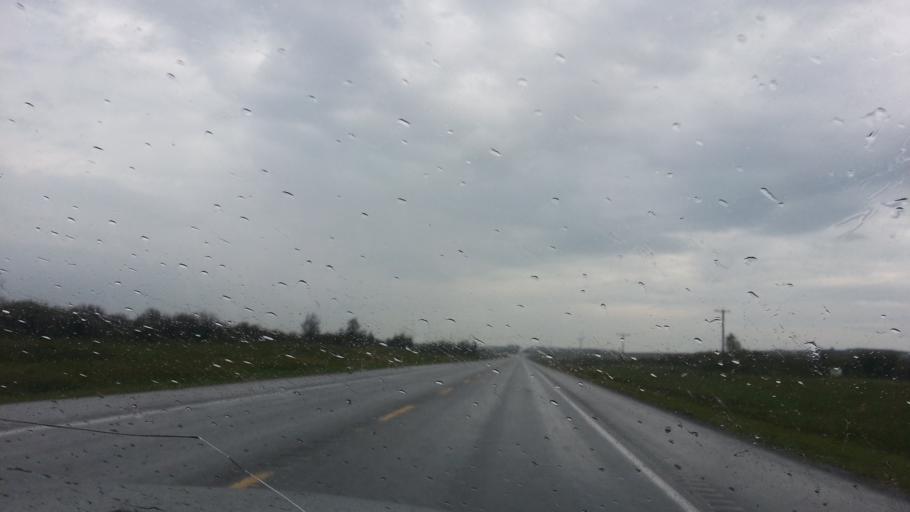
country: CA
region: Alberta
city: Cochrane
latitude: 51.0712
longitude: -114.4669
